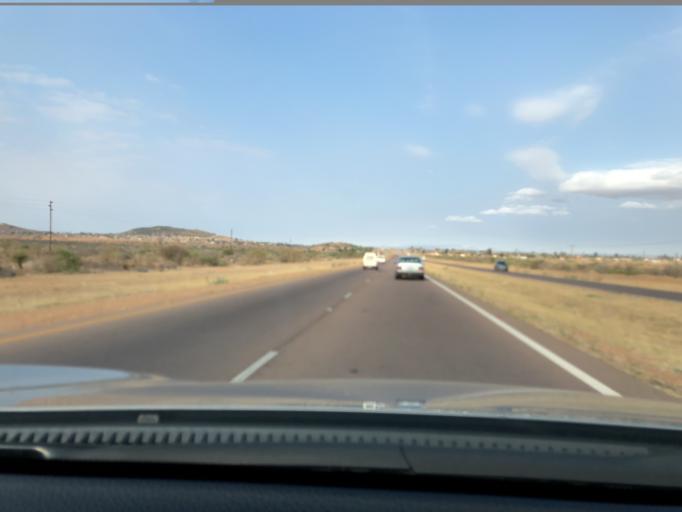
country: ZA
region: Limpopo
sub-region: Capricorn District Municipality
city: Polokwane
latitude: -23.8941
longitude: 29.6406
